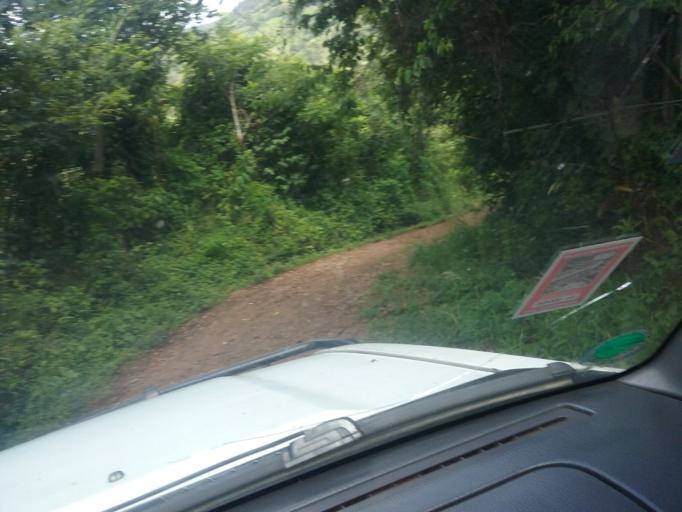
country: NI
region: Matagalpa
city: Matagalpa
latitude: 12.8664
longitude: -85.9147
